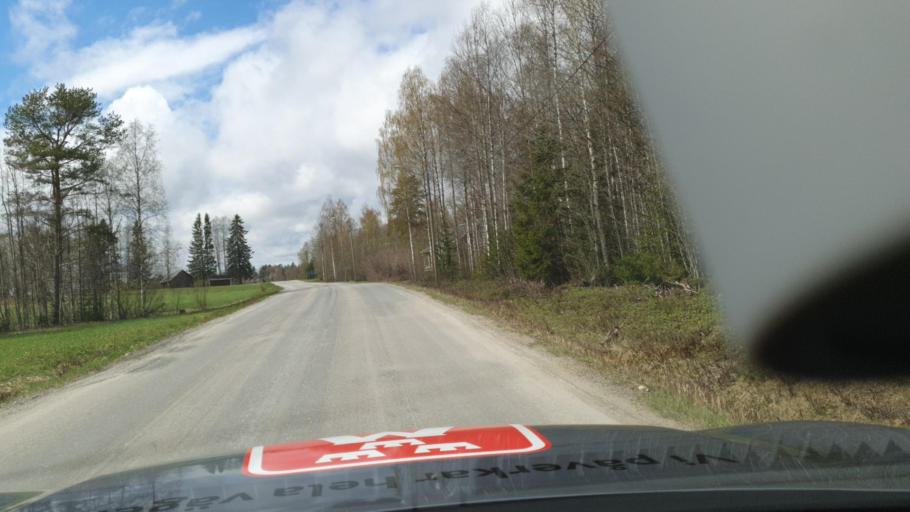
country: SE
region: Vaesterbotten
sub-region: Bjurholms Kommun
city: Bjurholm
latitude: 63.6956
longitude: 18.8848
